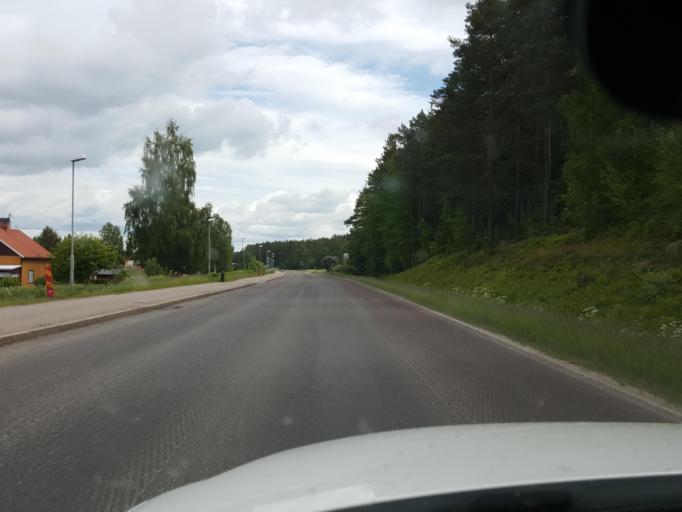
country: SE
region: Gaevleborg
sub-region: Ljusdals Kommun
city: Farila
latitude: 61.8012
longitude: 15.8542
